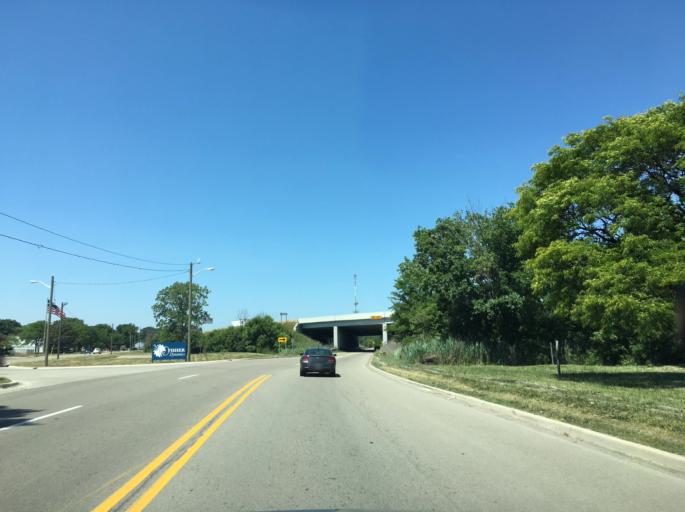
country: US
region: Michigan
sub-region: Macomb County
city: Saint Clair Shores
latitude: 42.5402
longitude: -82.8841
